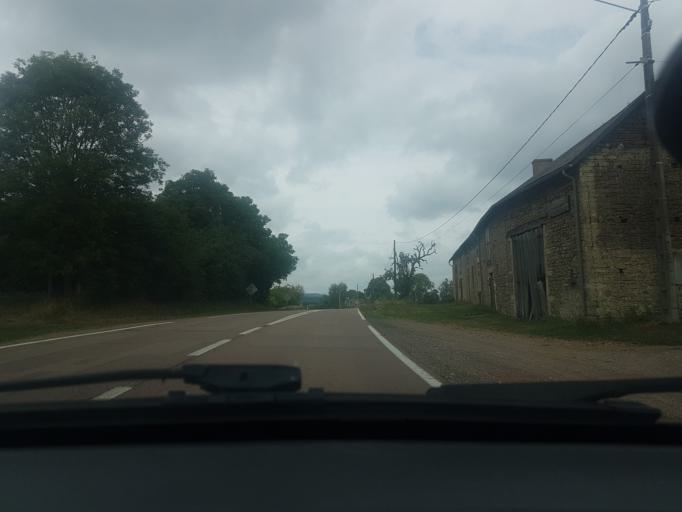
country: FR
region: Bourgogne
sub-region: Departement de la Cote-d'Or
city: Saulieu
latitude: 47.2253
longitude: 4.3229
